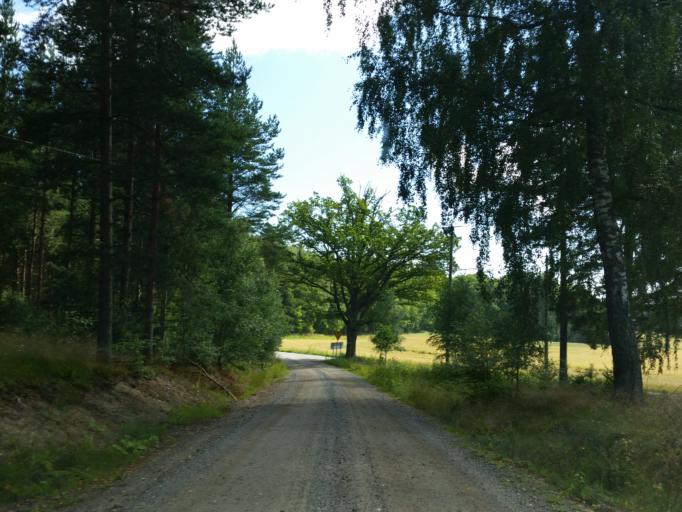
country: SE
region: Stockholm
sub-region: Sodertalje Kommun
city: Pershagen
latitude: 59.0584
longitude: 17.6549
